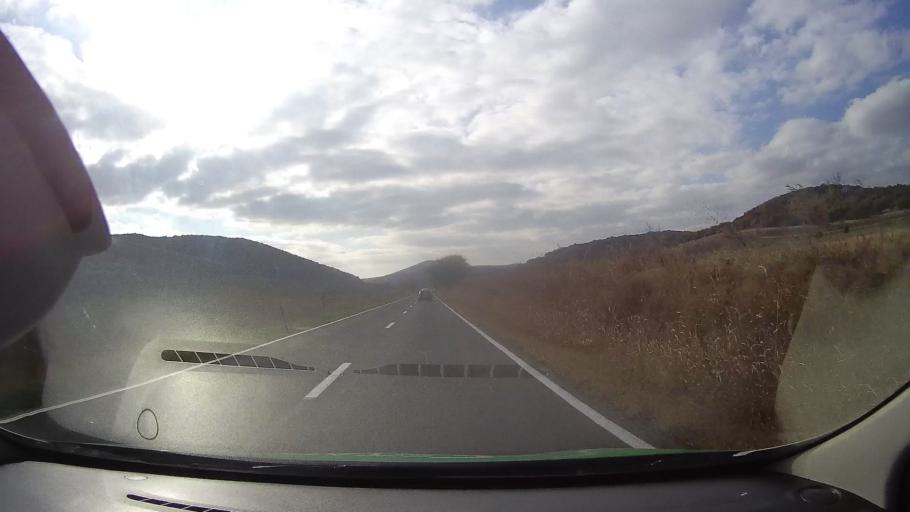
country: RO
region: Tulcea
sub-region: Comuna Nalbant
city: Nicolae Balcescu
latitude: 44.9676
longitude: 28.5340
